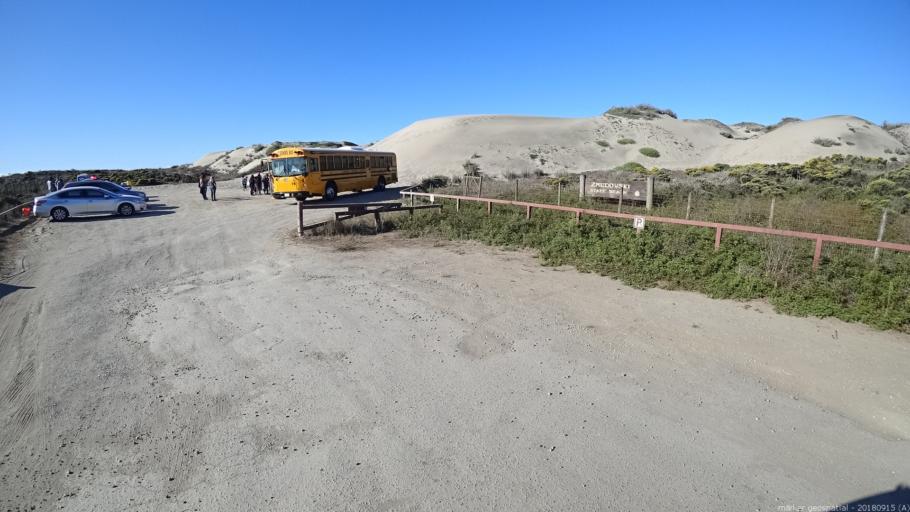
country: US
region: California
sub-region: Monterey County
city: Elkhorn
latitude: 36.8363
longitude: -121.8015
